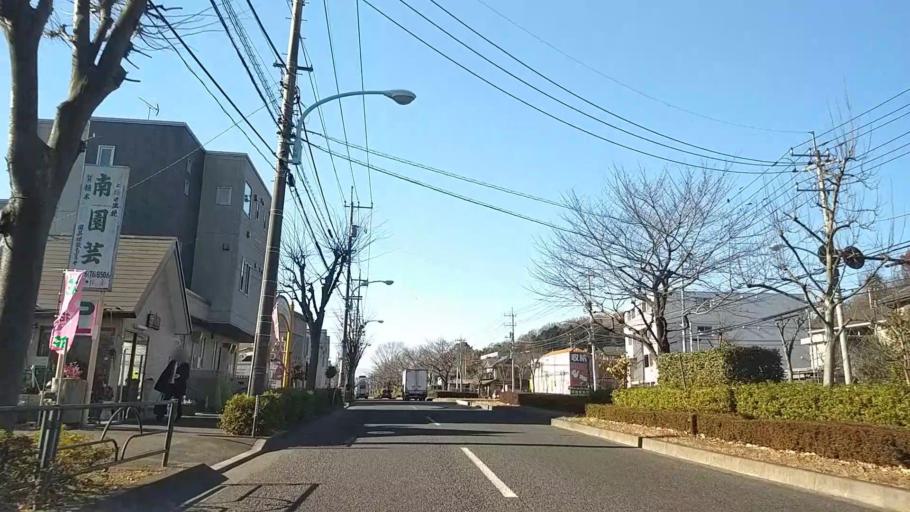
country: JP
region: Tokyo
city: Hino
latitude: 35.6364
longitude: 139.4130
